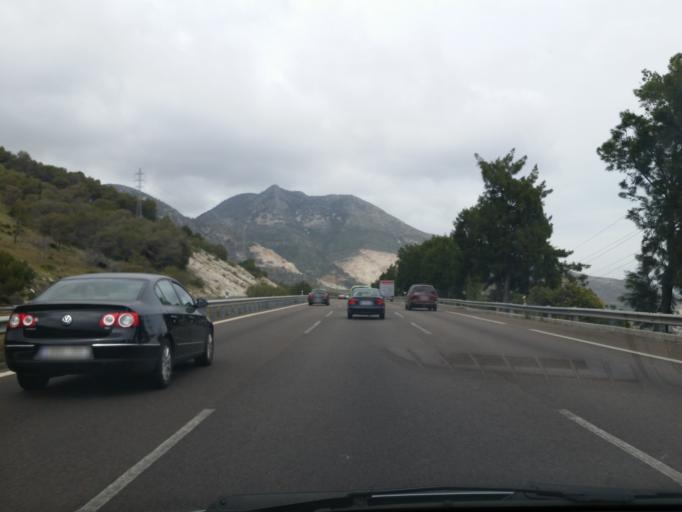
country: ES
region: Andalusia
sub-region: Provincia de Malaga
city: Benalmadena
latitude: 36.5948
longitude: -4.5776
